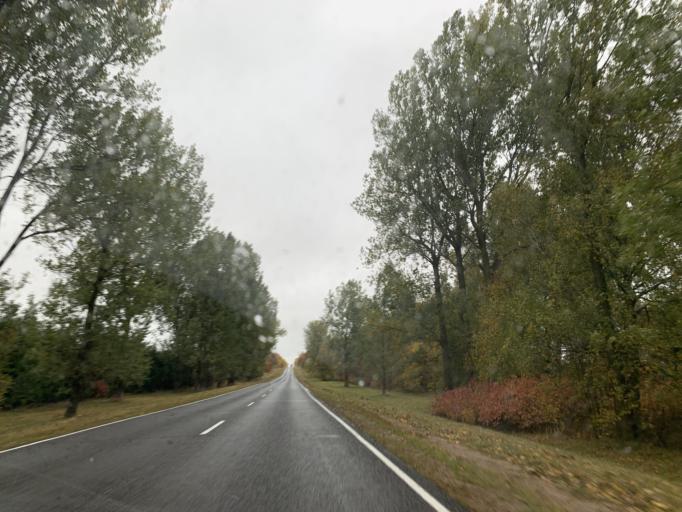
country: BY
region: Minsk
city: Novy Svyerzhan'
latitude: 53.4305
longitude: 26.6421
